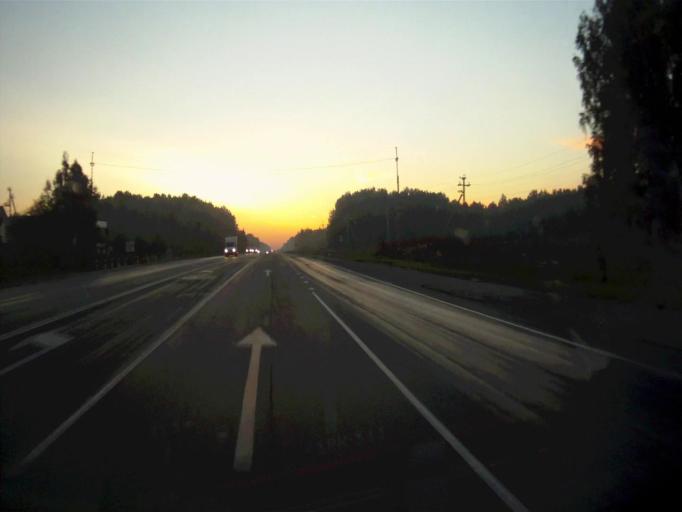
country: RU
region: Chelyabinsk
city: Poletayevo
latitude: 55.2045
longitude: 61.1166
